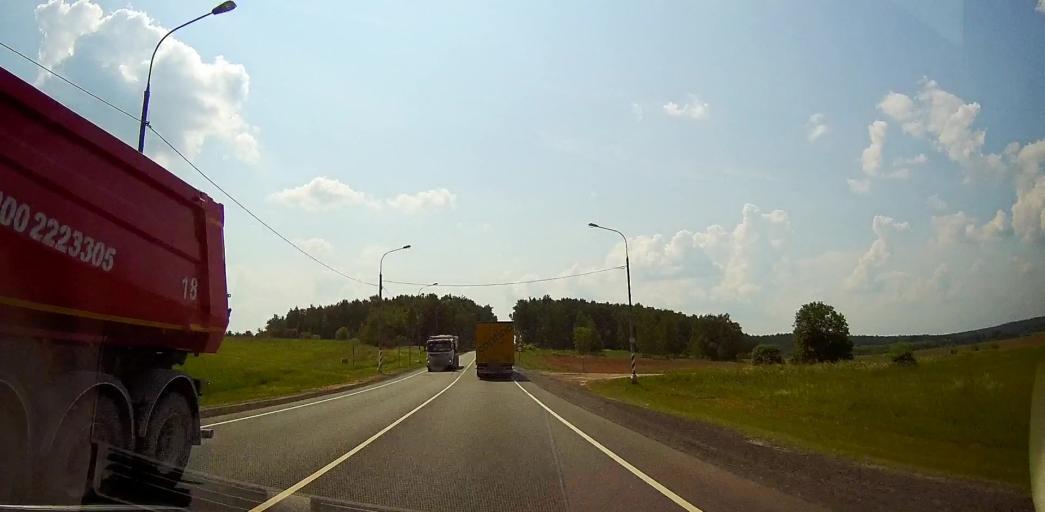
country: RU
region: Moskovskaya
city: Meshcherino
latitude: 55.1841
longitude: 38.3538
